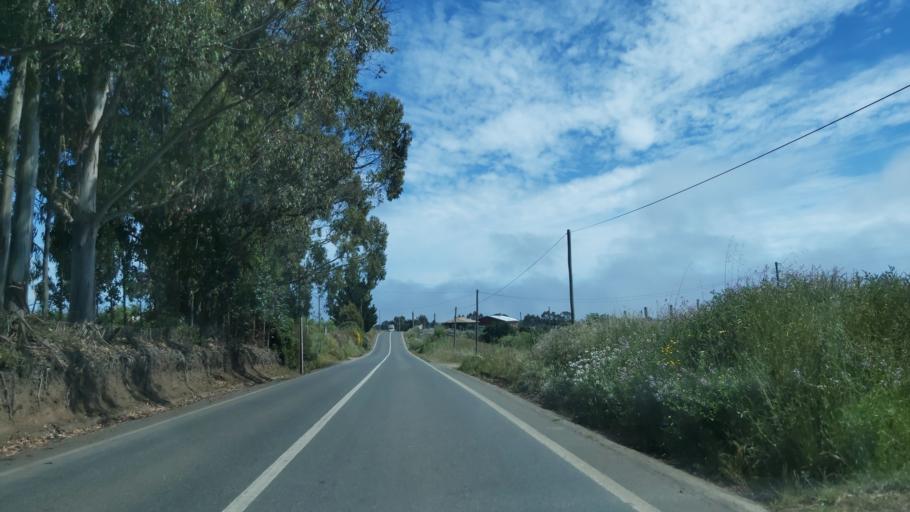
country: CL
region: Maule
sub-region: Provincia de Talca
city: Constitucion
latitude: -35.5801
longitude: -72.6013
